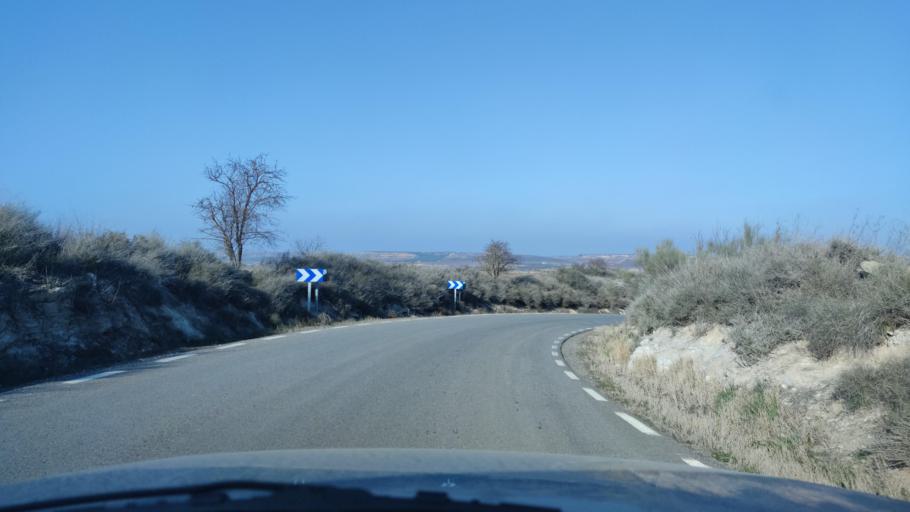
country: ES
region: Catalonia
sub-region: Provincia de Lleida
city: Sunyer
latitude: 41.4972
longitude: 0.5603
